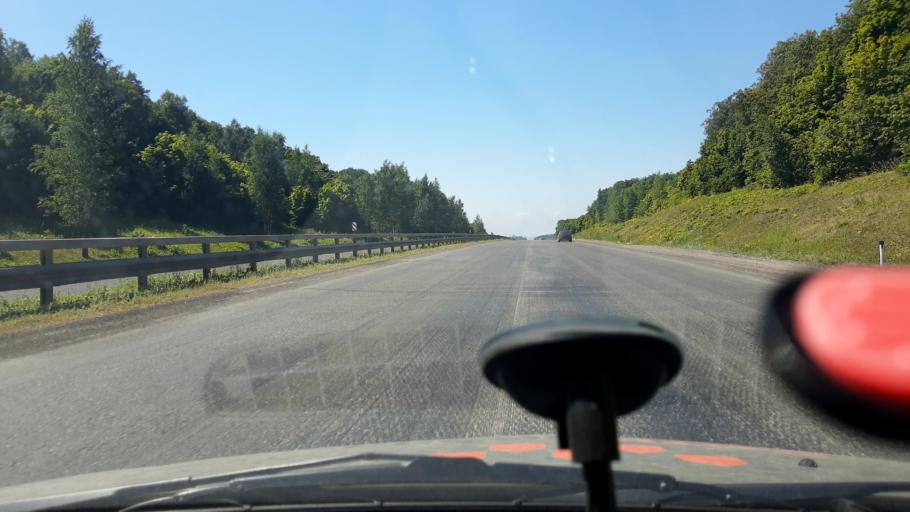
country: RU
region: Bashkortostan
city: Avdon
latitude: 54.6533
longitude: 55.6778
